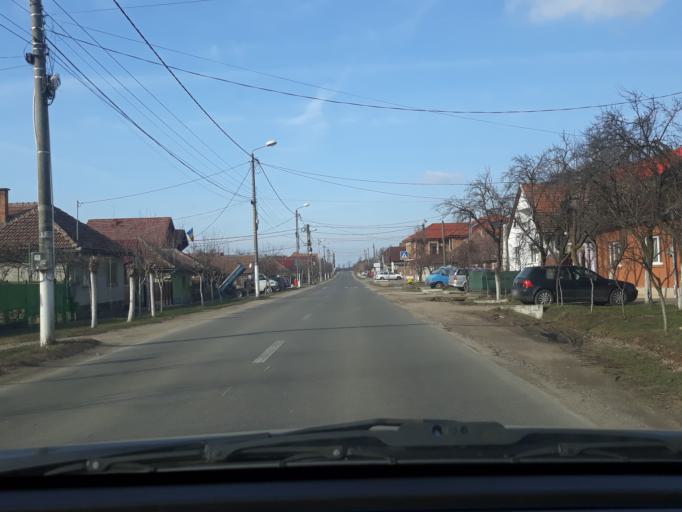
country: RO
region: Bihor
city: Margita
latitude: 47.3586
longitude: 22.3348
